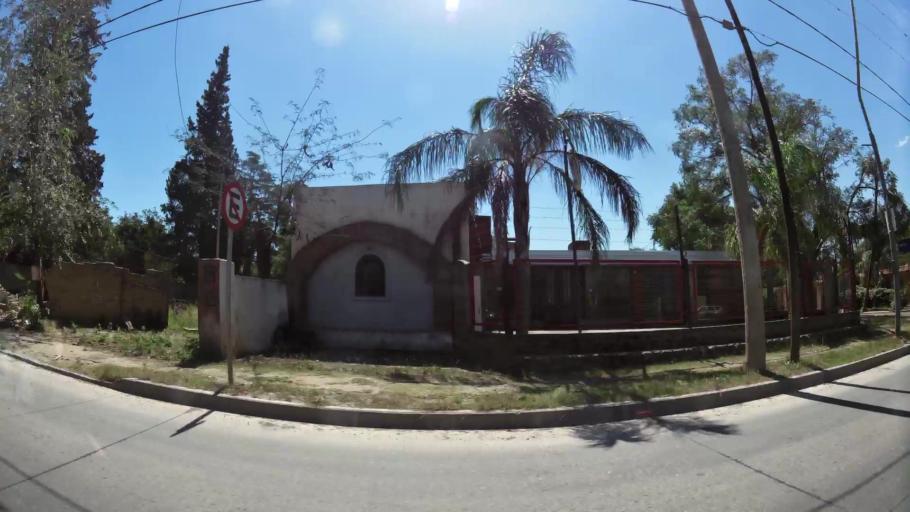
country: AR
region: Cordoba
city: Saldan
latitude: -31.3370
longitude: -64.2811
